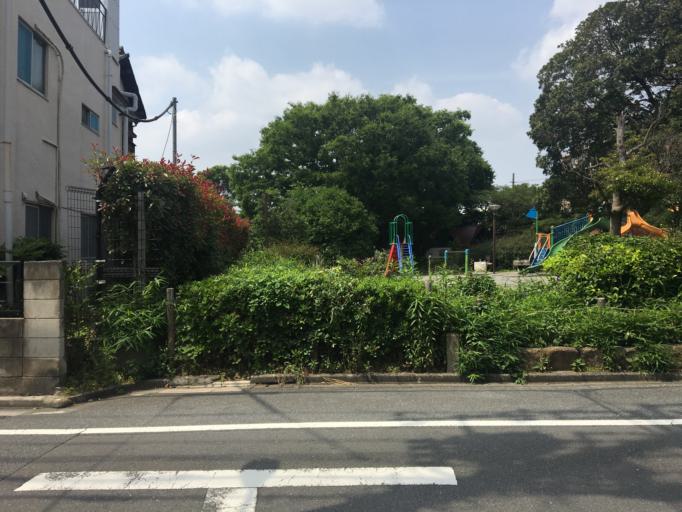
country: JP
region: Tokyo
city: Tokyo
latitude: 35.7307
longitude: 139.6936
